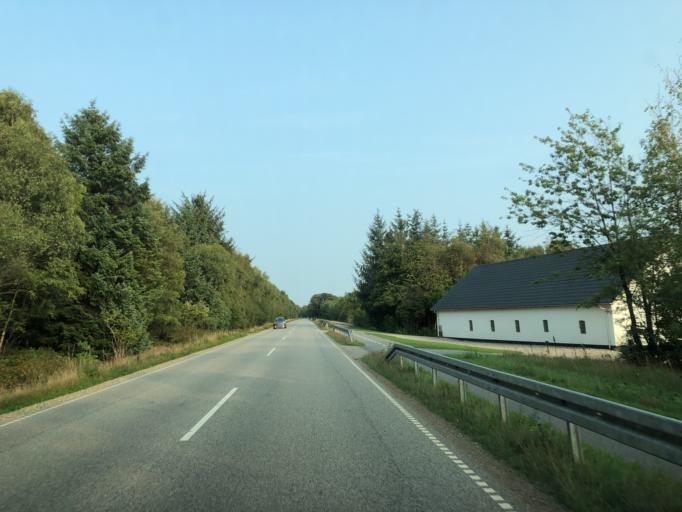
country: DK
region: South Denmark
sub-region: Billund Kommune
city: Grindsted
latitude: 55.8205
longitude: 9.0049
